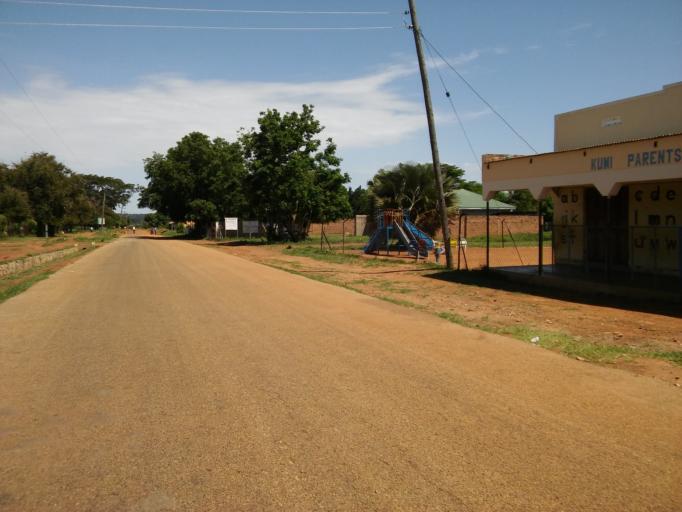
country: UG
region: Eastern Region
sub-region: Kumi District
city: Kumi
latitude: 1.4863
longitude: 33.9247
